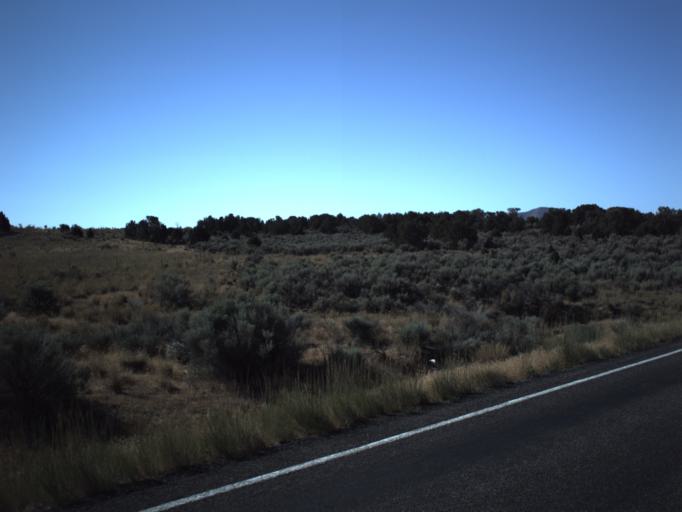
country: US
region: Utah
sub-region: Juab County
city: Mona
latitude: 39.7428
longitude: -112.1876
